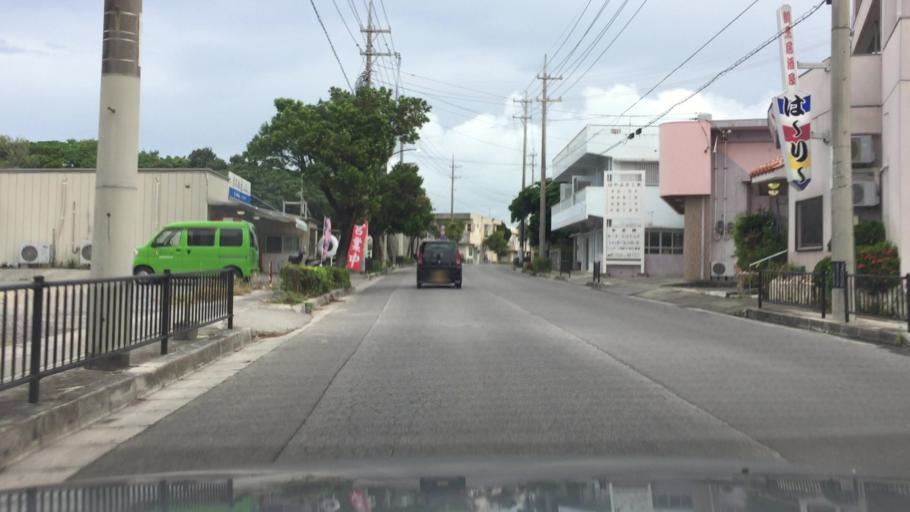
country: JP
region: Okinawa
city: Ishigaki
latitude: 24.3478
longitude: 124.1578
